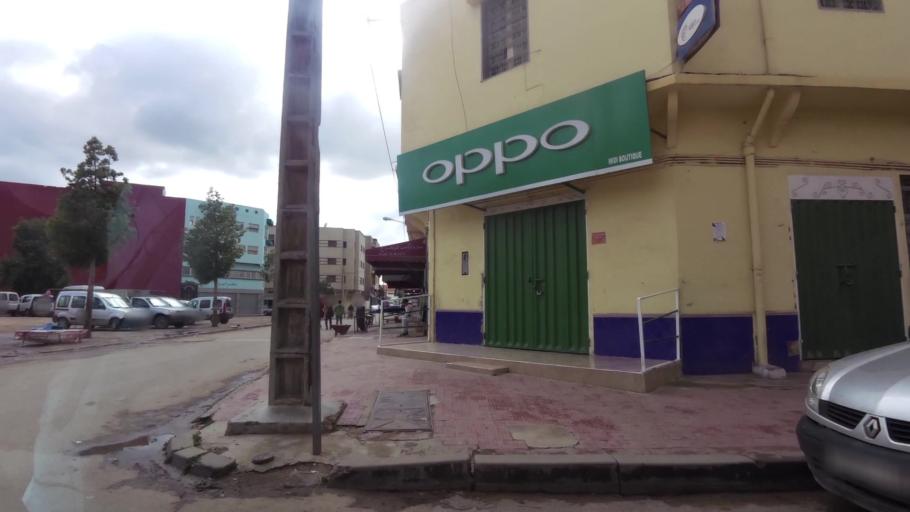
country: MA
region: Chaouia-Ouardigha
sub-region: Settat Province
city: Berrechid
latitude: 33.2669
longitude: -7.5869
